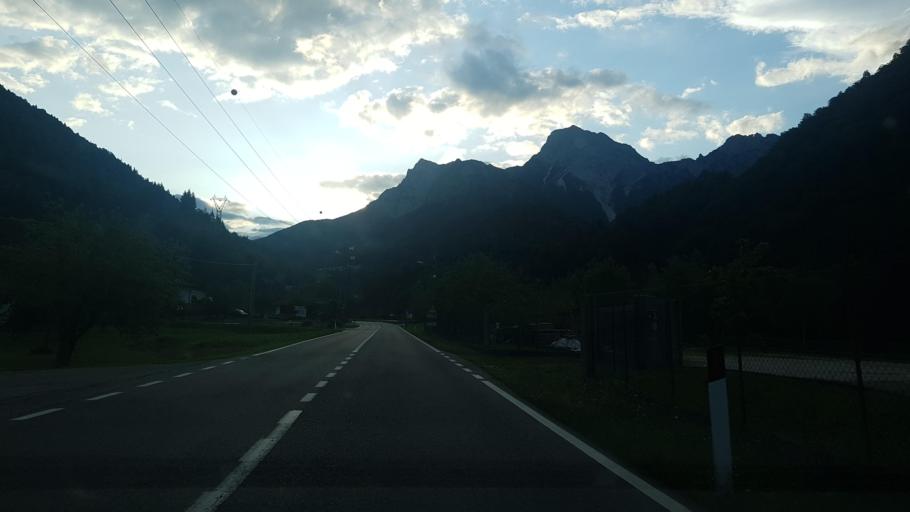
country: IT
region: Friuli Venezia Giulia
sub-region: Provincia di Udine
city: Zuglio
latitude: 46.4689
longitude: 13.0627
